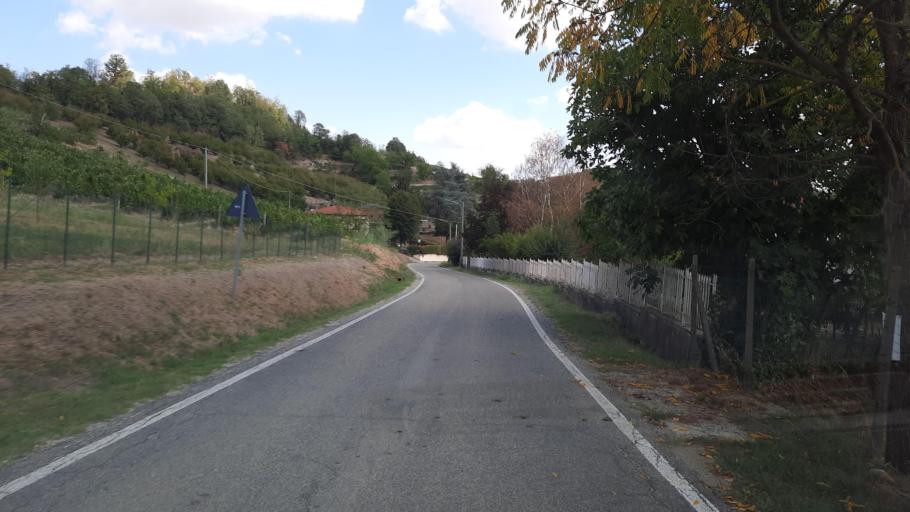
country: IT
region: Piedmont
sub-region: Provincia di Alessandria
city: Ottiglio
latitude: 45.0588
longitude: 8.3423
